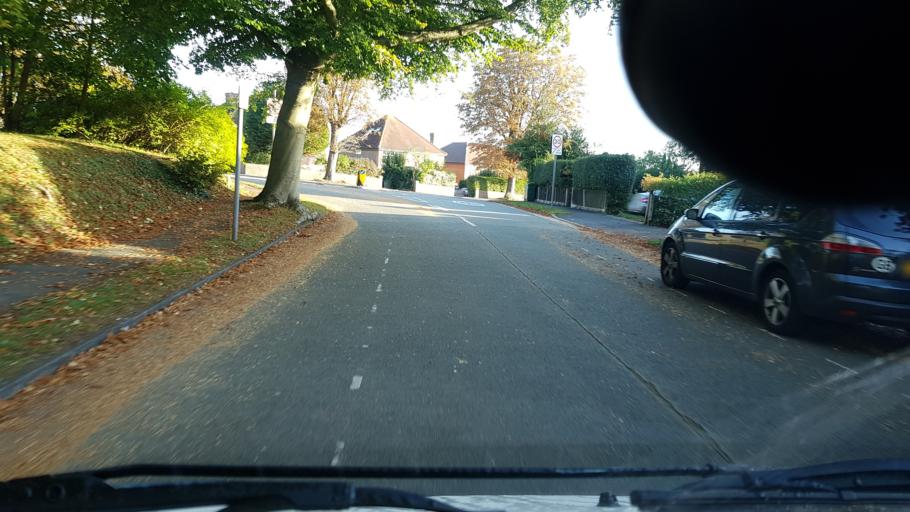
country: GB
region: England
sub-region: Surrey
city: Guildford
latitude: 51.2333
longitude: -0.5894
